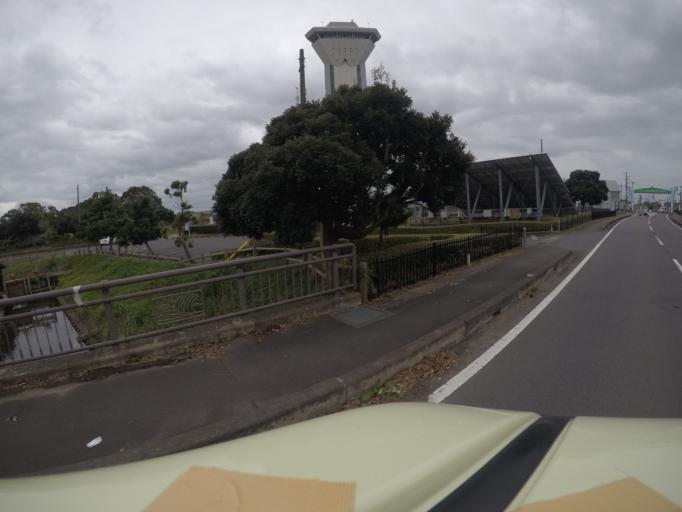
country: JP
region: Ibaraki
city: Ishioka
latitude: 36.0977
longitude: 140.4039
